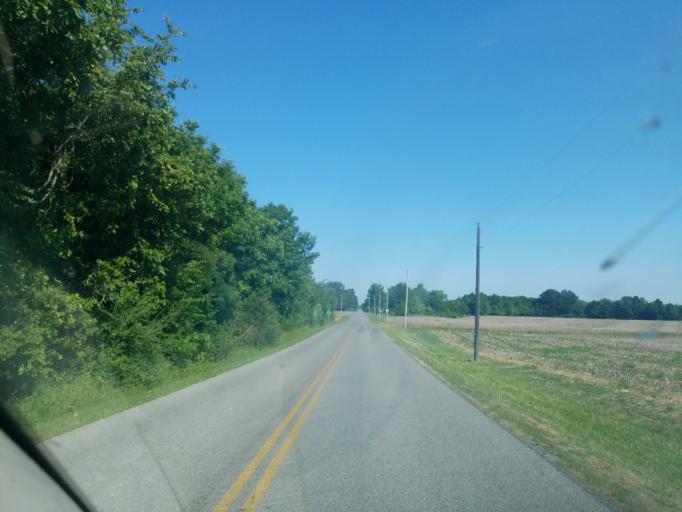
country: US
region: Ohio
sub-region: Logan County
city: Northwood
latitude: 40.4262
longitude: -83.7052
